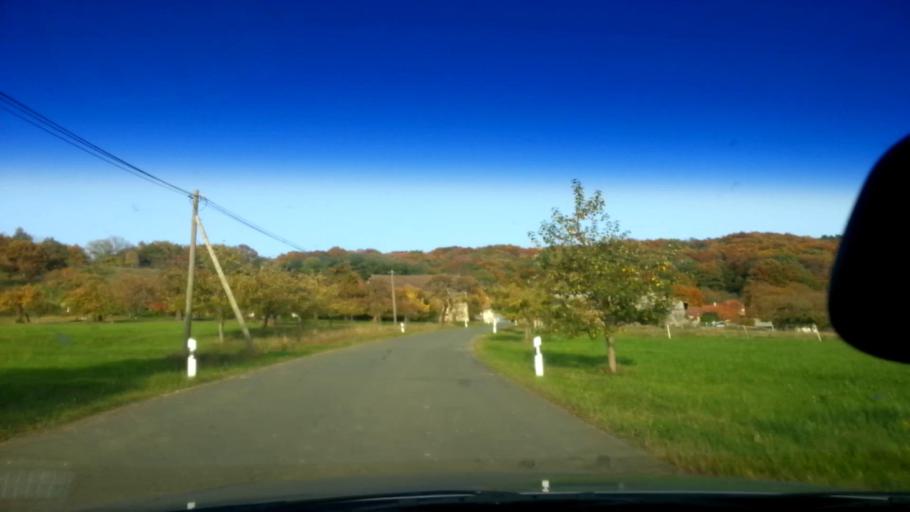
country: DE
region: Bavaria
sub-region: Upper Franconia
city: Schesslitz
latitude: 50.0167
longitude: 11.0219
